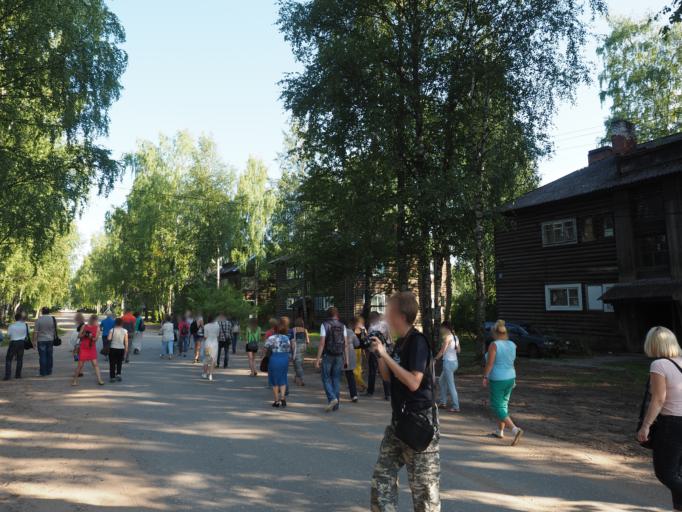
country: RU
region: Vologda
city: Chagoda
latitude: 59.1676
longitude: 35.3265
